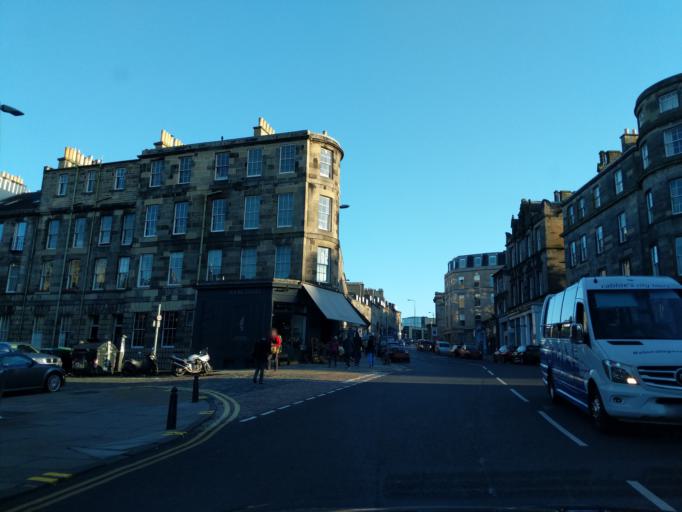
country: GB
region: Scotland
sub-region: Edinburgh
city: Edinburgh
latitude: 55.9586
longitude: -3.1899
